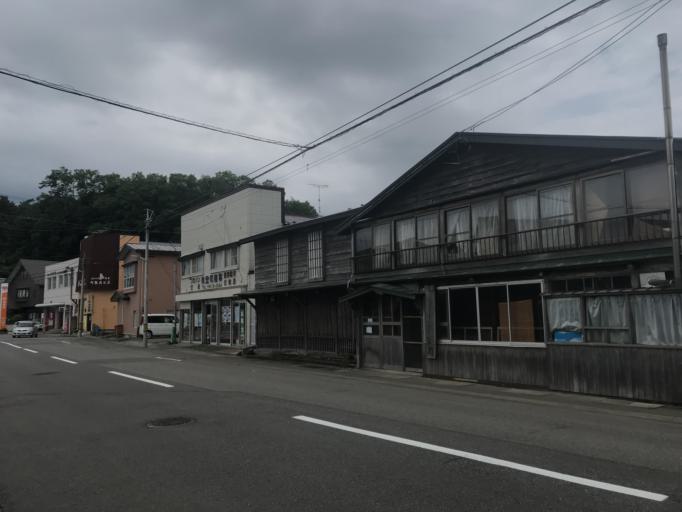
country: JP
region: Aomori
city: Shimokizukuri
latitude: 40.7835
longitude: 140.2048
